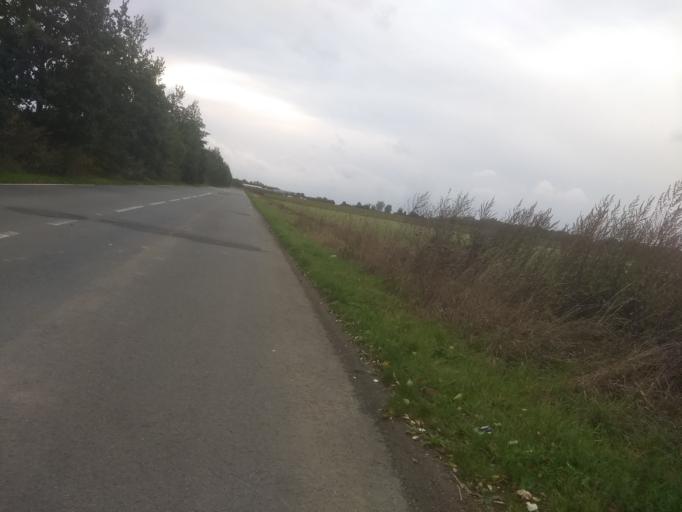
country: FR
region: Nord-Pas-de-Calais
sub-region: Departement du Pas-de-Calais
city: Achicourt
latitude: 50.2713
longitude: 2.7440
